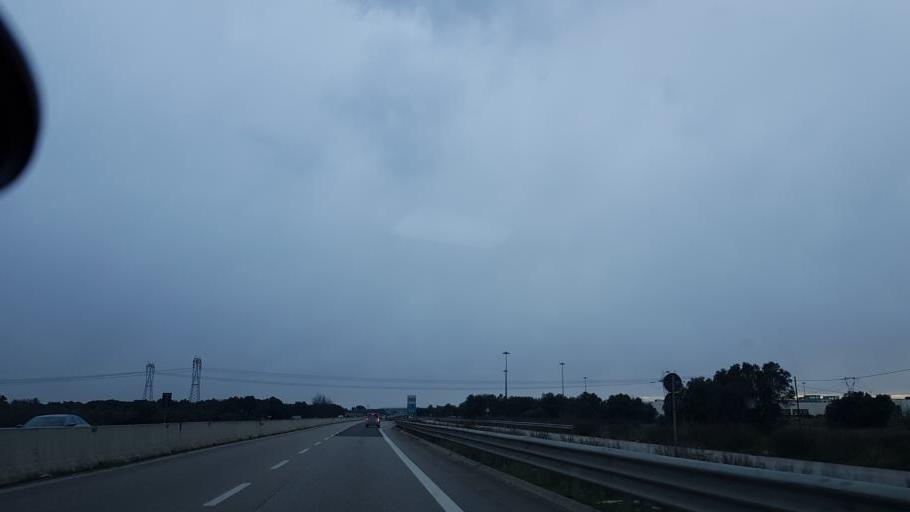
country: IT
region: Apulia
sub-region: Provincia di Brindisi
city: Mesagne
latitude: 40.5806
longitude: 17.8419
